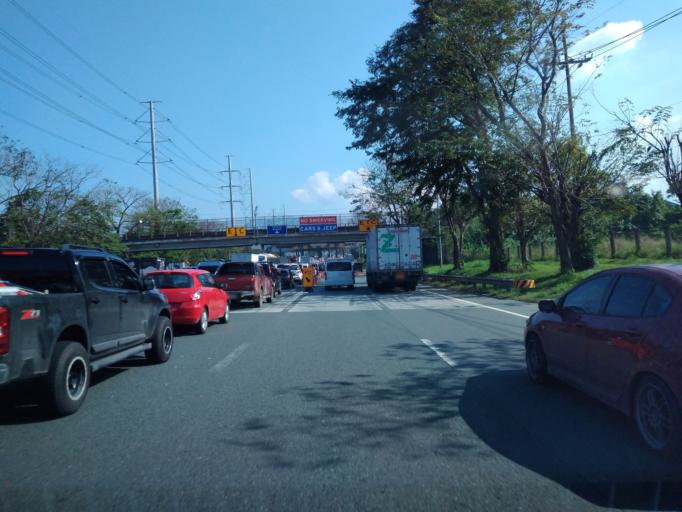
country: PH
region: Calabarzon
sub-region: Province of Laguna
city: Prinza
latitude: 14.2221
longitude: 121.1233
